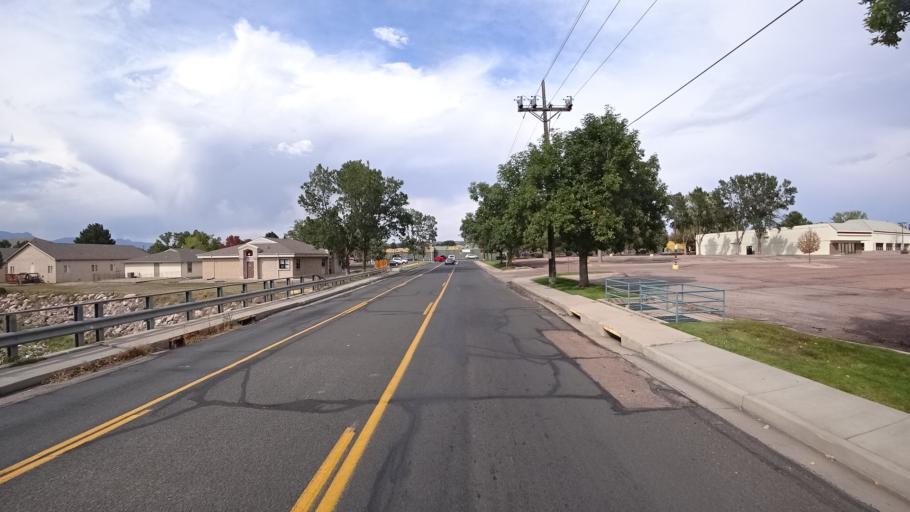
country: US
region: Colorado
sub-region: El Paso County
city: Cimarron Hills
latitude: 38.8885
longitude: -104.7609
